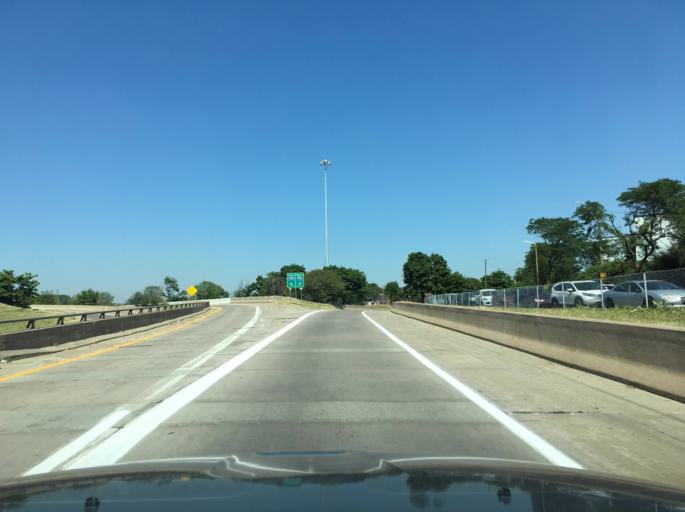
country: US
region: Michigan
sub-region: Wayne County
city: Detroit
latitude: 42.3448
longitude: -83.0424
